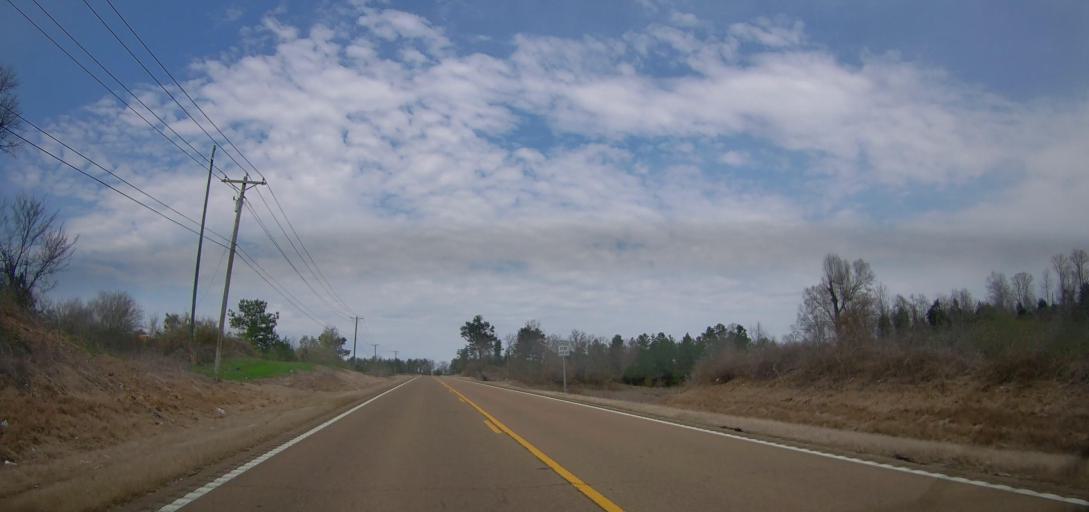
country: US
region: Mississippi
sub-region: Marshall County
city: Holly Springs
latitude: 34.7481
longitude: -89.4280
